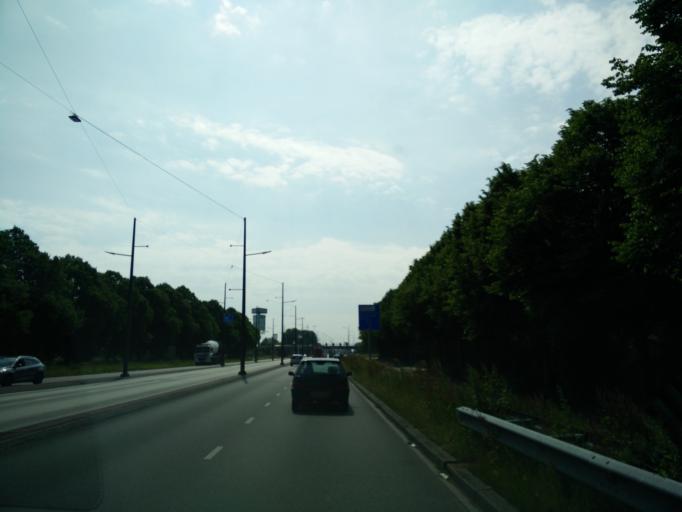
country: NL
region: Groningen
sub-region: Gemeente Groningen
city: Oosterpark
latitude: 53.2135
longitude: 6.5849
